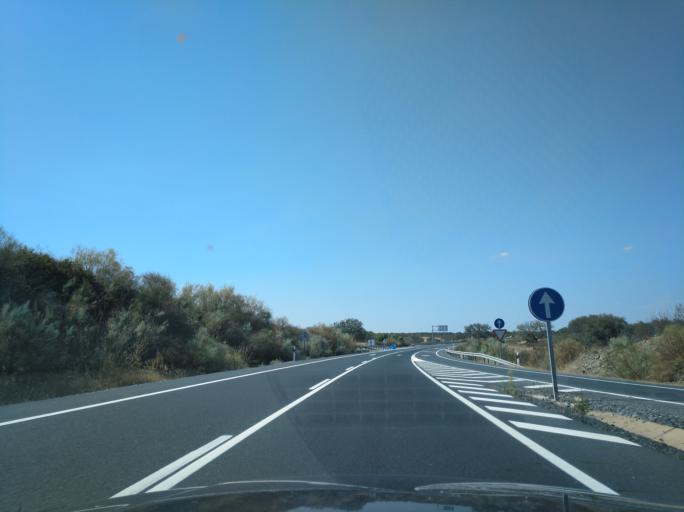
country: ES
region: Andalusia
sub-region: Provincia de Huelva
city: San Bartolome de la Torre
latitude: 37.4479
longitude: -7.1262
